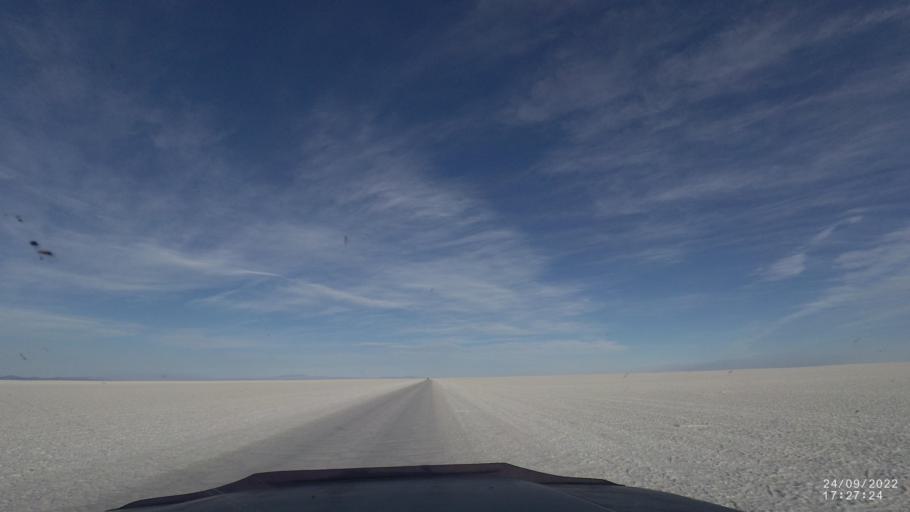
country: BO
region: Potosi
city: Colchani
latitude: -20.2998
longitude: -67.4494
